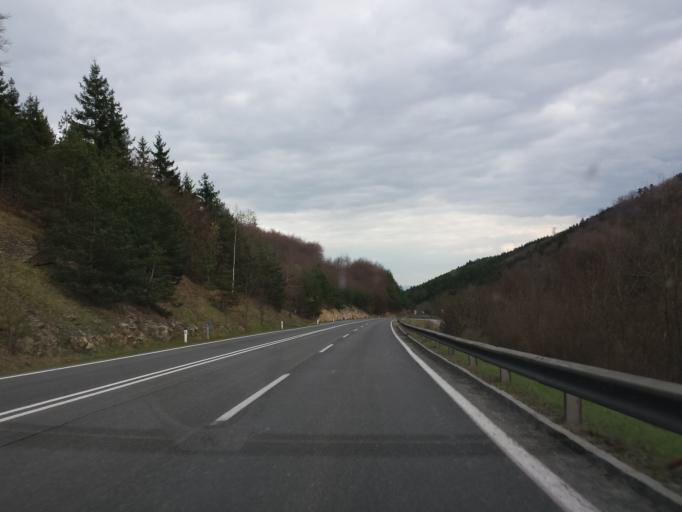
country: AT
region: Lower Austria
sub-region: Politischer Bezirk Krems
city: Lengenfeld
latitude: 48.4996
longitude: 15.5570
